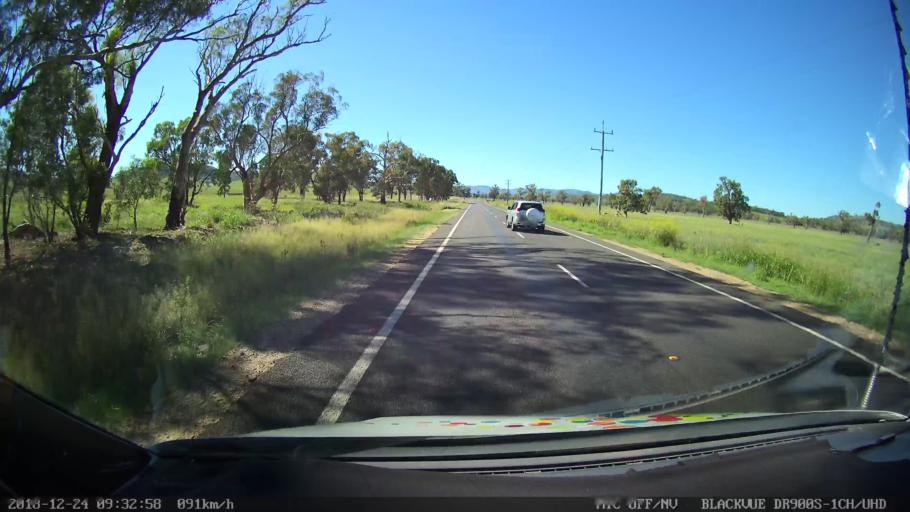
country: AU
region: New South Wales
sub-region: Liverpool Plains
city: Quirindi
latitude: -31.5973
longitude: 150.7046
